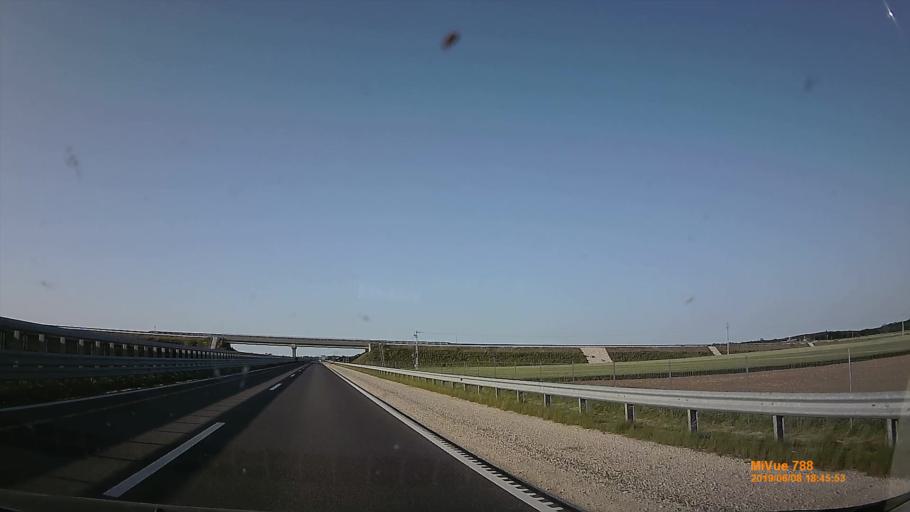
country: HU
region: Gyor-Moson-Sopron
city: Beled
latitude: 47.4857
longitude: 17.1471
